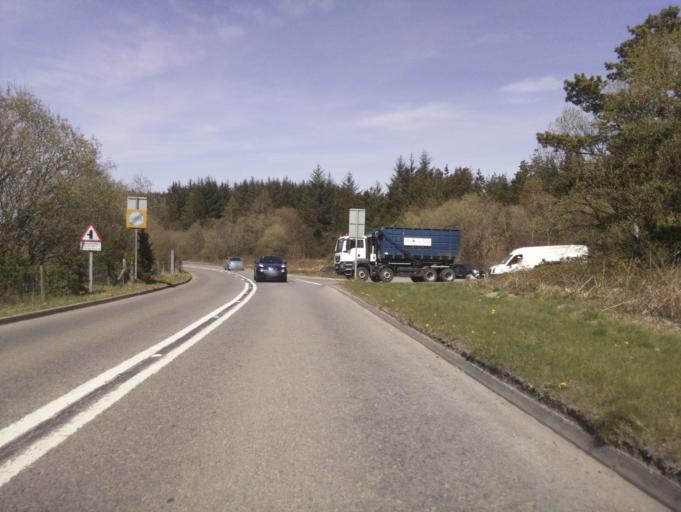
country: GB
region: Wales
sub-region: Rhondda Cynon Taf
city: Aberdare
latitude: 51.7471
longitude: -3.4420
